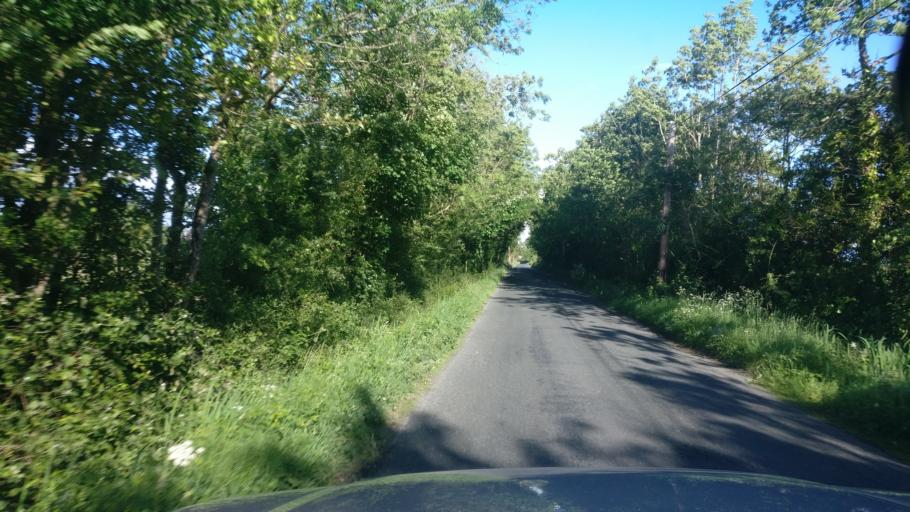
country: IE
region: Connaught
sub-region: County Galway
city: Ballinasloe
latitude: 53.2293
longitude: -8.2437
